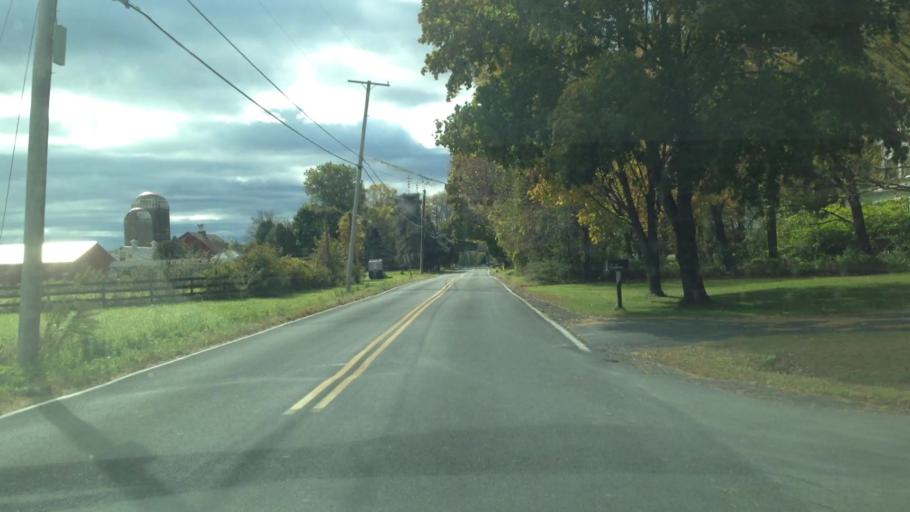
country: US
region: New York
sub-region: Ulster County
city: New Paltz
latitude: 41.7894
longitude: -74.0872
